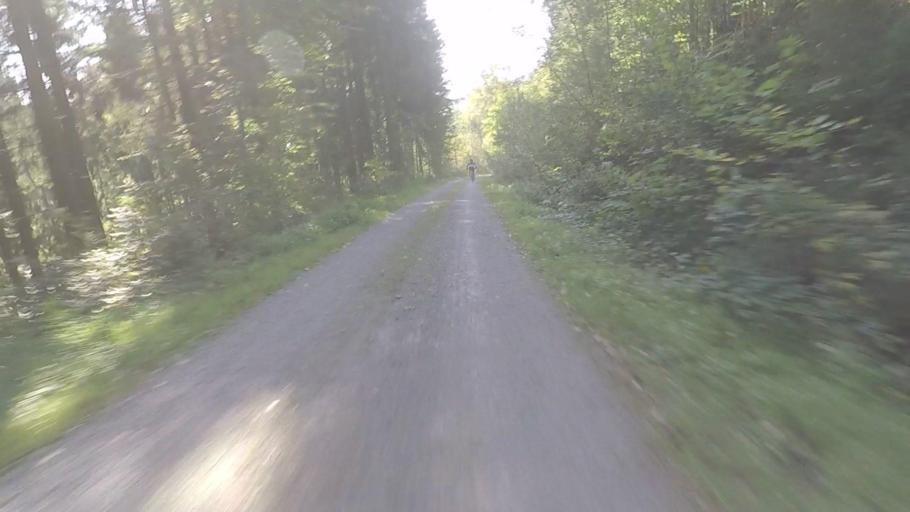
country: DE
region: Baden-Wuerttemberg
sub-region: Regierungsbezirk Stuttgart
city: Spiegelberg
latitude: 49.0242
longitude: 9.4675
